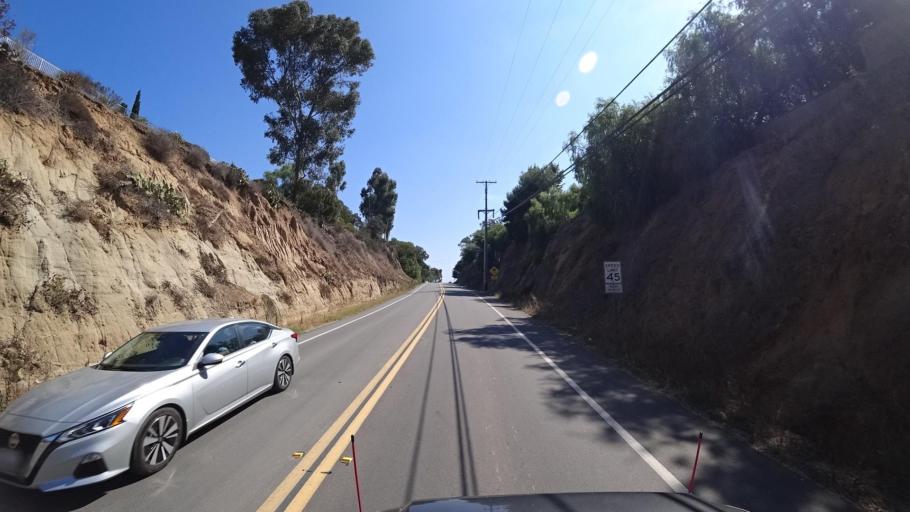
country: US
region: California
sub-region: San Diego County
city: Fairbanks Ranch
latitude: 32.9835
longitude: -117.2233
